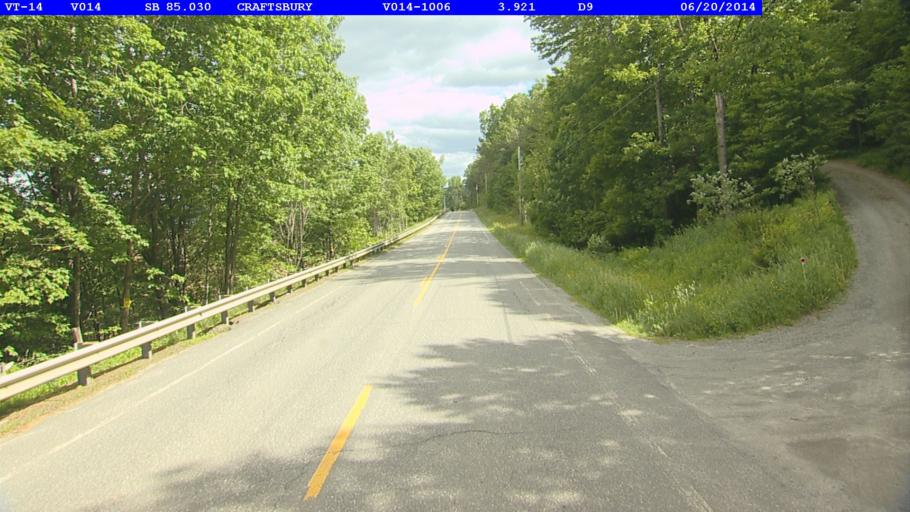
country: US
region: Vermont
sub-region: Caledonia County
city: Hardwick
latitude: 44.6474
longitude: -72.4040
